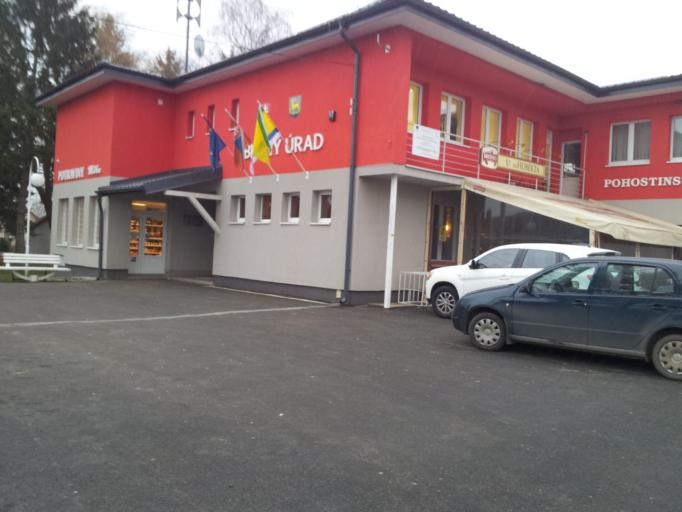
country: SK
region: Presovsky
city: Vranov nad Topl'ou
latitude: 48.9697
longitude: 21.7105
